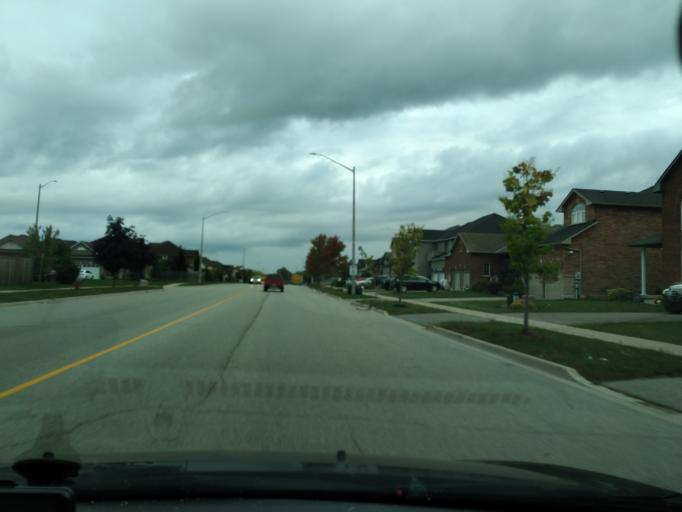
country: CA
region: Ontario
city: Innisfil
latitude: 44.3079
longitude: -79.5574
